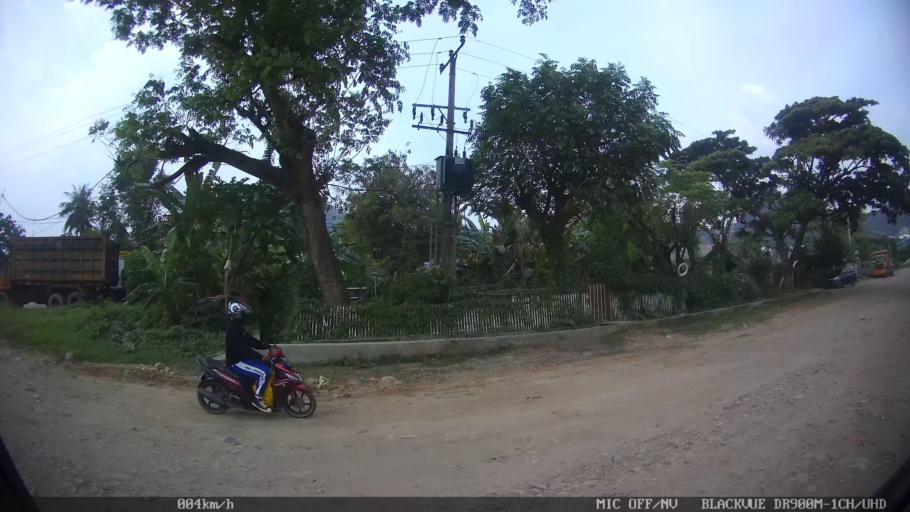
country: ID
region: Lampung
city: Panjang
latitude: -5.4457
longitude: 105.3074
